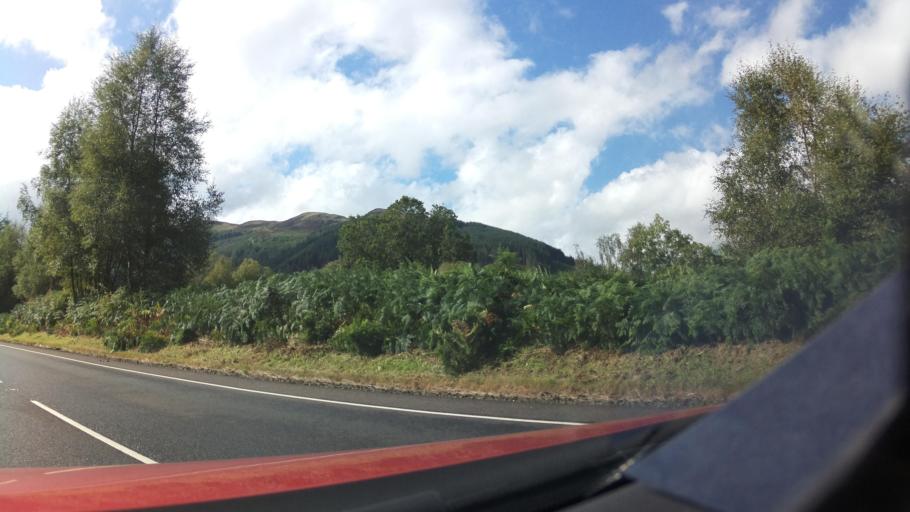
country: GB
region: Scotland
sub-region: Stirling
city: Callander
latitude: 56.3516
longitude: -4.3285
